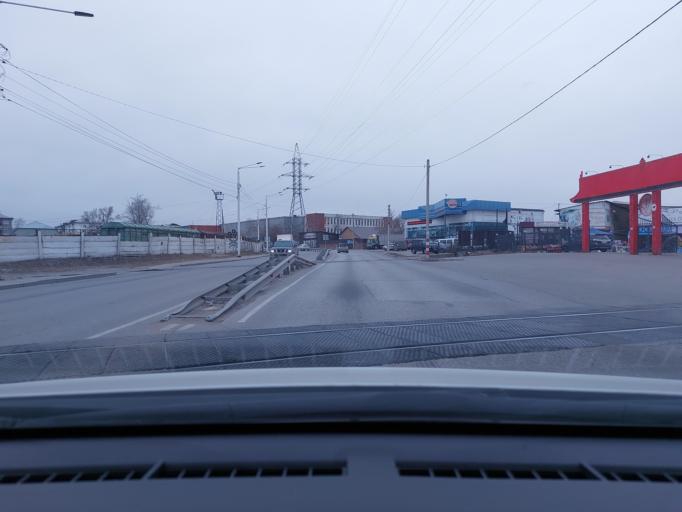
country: RU
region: Irkutsk
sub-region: Irkutskiy Rayon
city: Irkutsk
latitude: 52.3376
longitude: 104.2328
